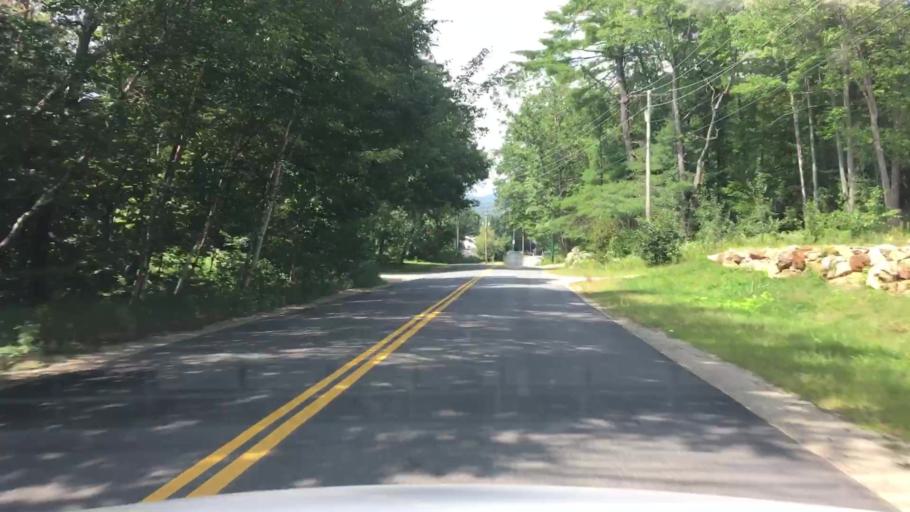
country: US
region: Maine
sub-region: Oxford County
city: Rumford
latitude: 44.5190
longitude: -70.5267
